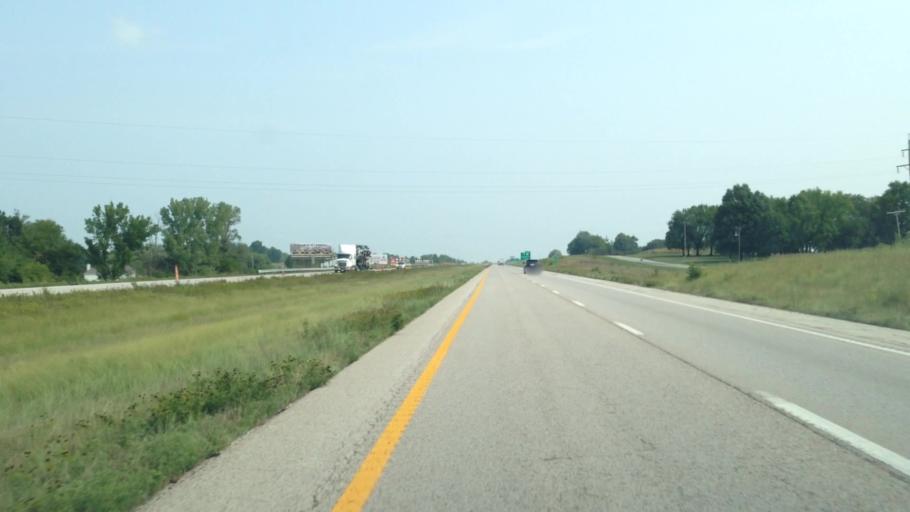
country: US
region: Missouri
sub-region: Clinton County
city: Cameron
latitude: 39.7116
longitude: -94.2246
